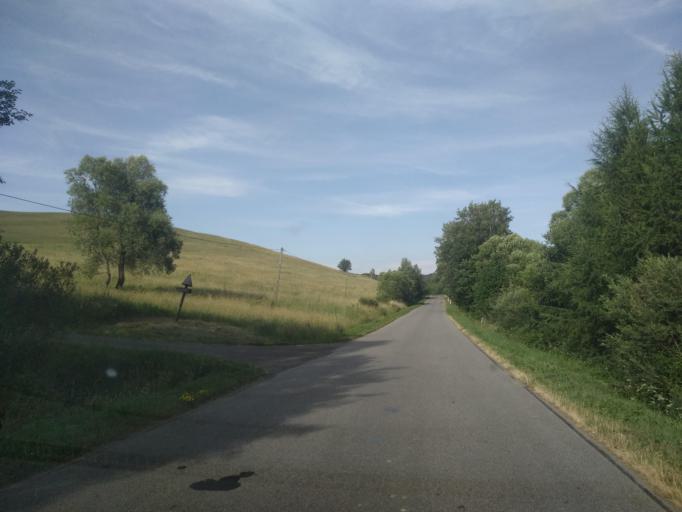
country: PL
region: Subcarpathian Voivodeship
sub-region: Powiat sanocki
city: Rzepedz
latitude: 49.4301
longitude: 22.1364
